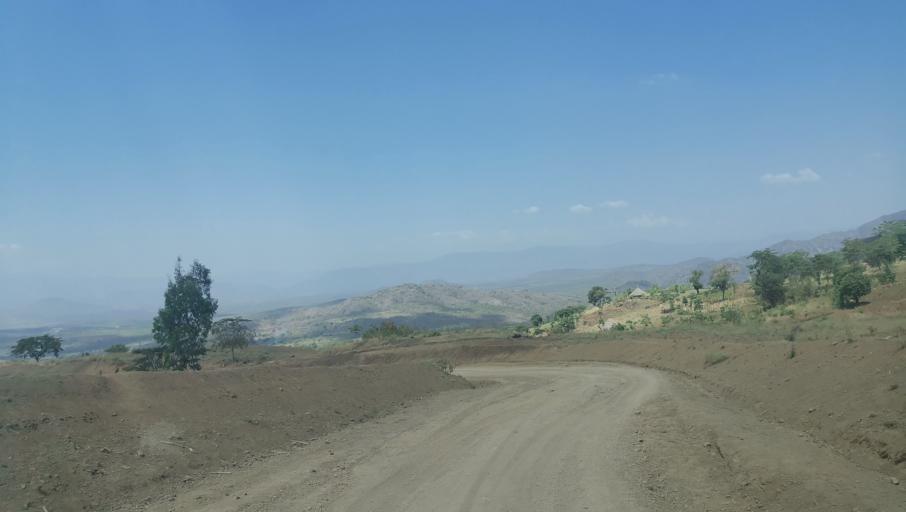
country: ET
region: Southern Nations, Nationalities, and People's Region
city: Arba Minch'
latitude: 6.3310
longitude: 37.3368
